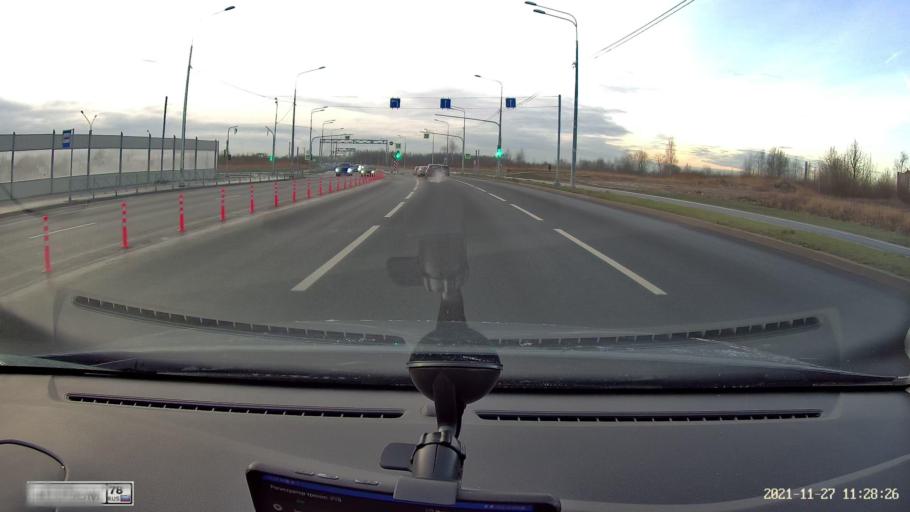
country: RU
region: St.-Petersburg
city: Krasnoye Selo
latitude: 59.7453
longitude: 30.0746
